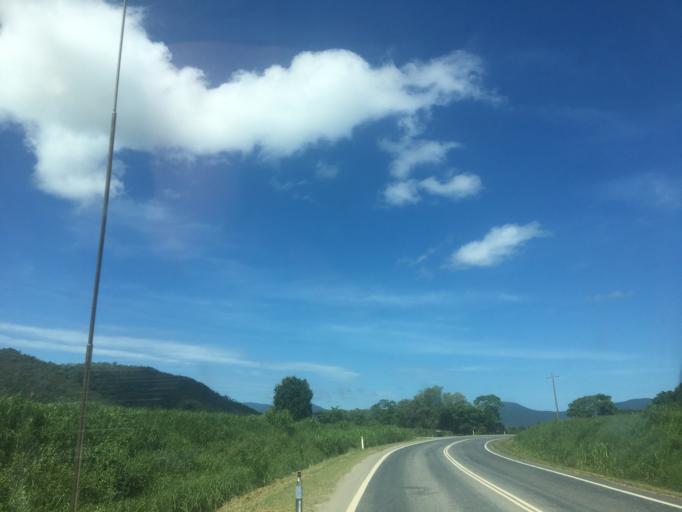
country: AU
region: Queensland
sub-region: Cairns
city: Woree
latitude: -17.0679
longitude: 145.7477
